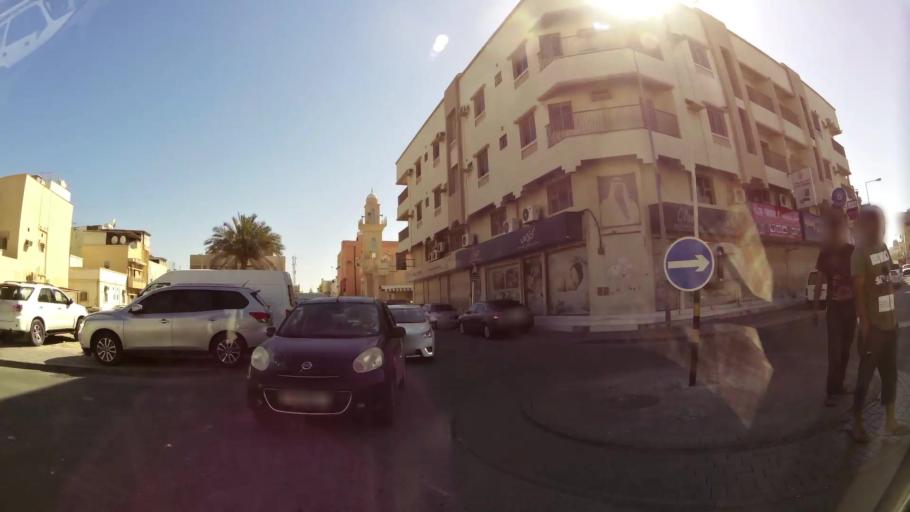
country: BH
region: Muharraq
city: Al Muharraq
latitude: 26.2563
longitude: 50.6169
